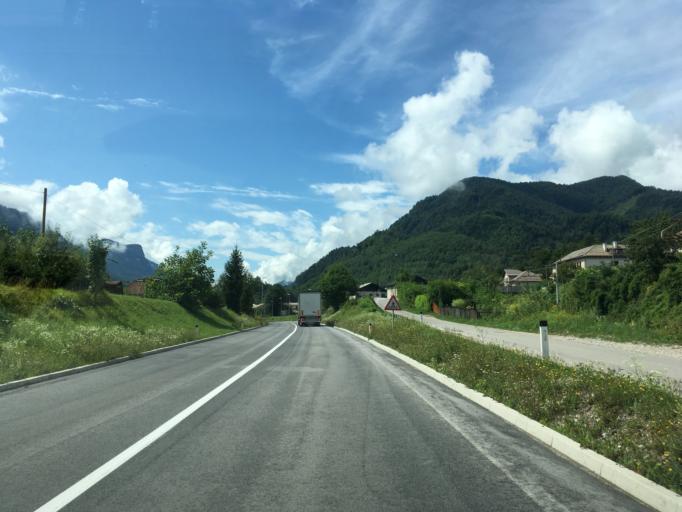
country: SI
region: Jesenice
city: Slovenski Javornik
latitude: 46.4247
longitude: 14.0990
